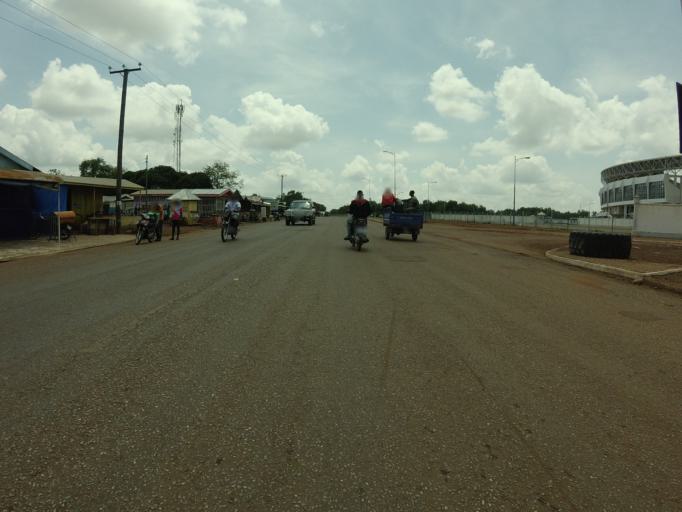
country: GH
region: Northern
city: Tamale
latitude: 9.4083
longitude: -0.8624
